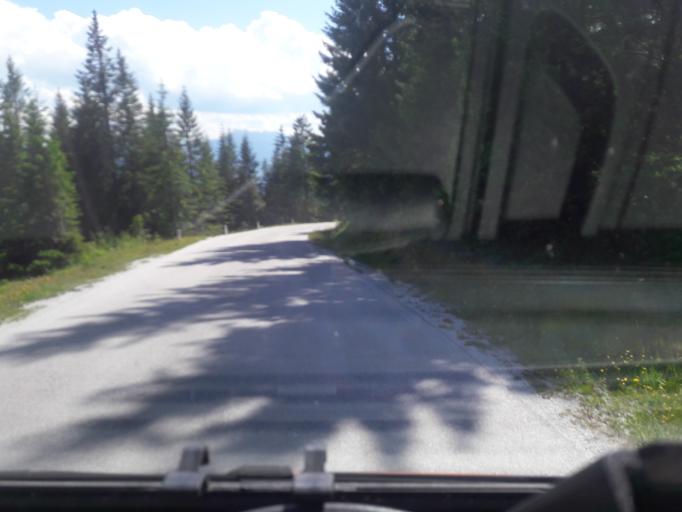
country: AT
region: Styria
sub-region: Politischer Bezirk Liezen
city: Tauplitz
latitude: 47.5849
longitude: 13.9674
